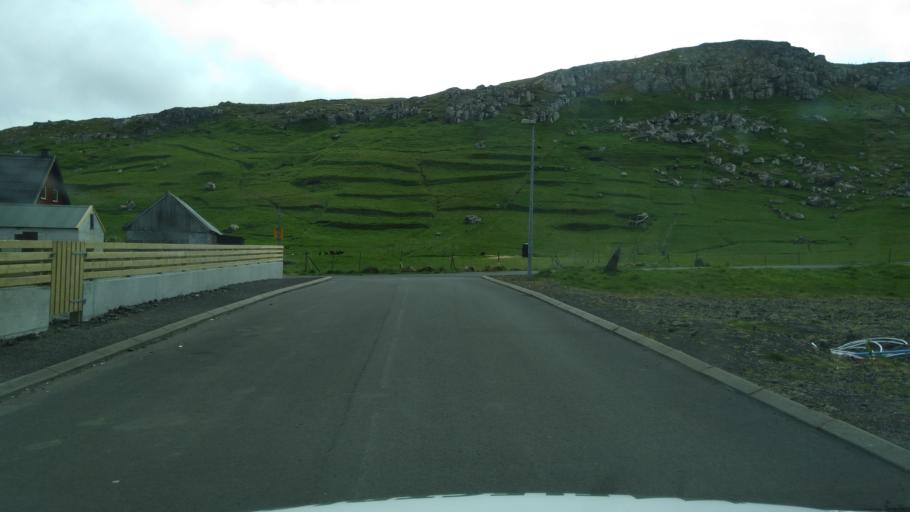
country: FO
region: Sandoy
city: Sandur
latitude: 61.9040
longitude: -6.8924
